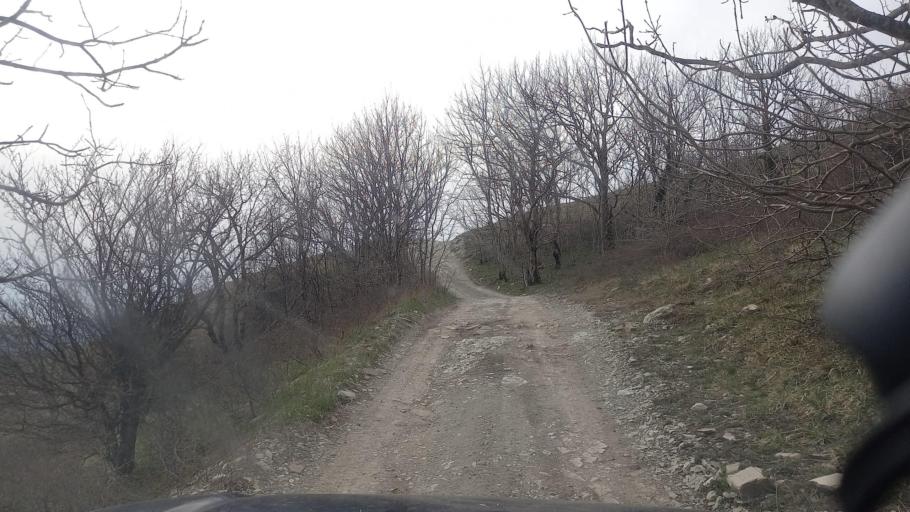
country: RU
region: Krasnodarskiy
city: Divnomorskoye
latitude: 44.6103
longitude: 38.2408
